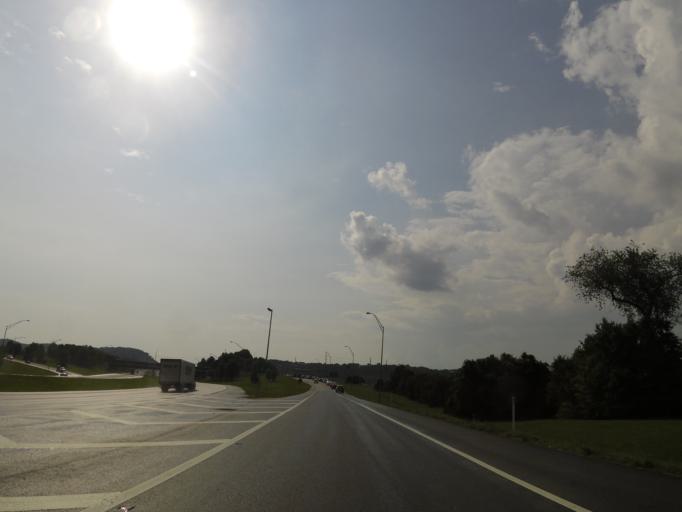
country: US
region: Tennessee
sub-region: Knox County
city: Knoxville
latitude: 36.0298
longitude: -83.8675
